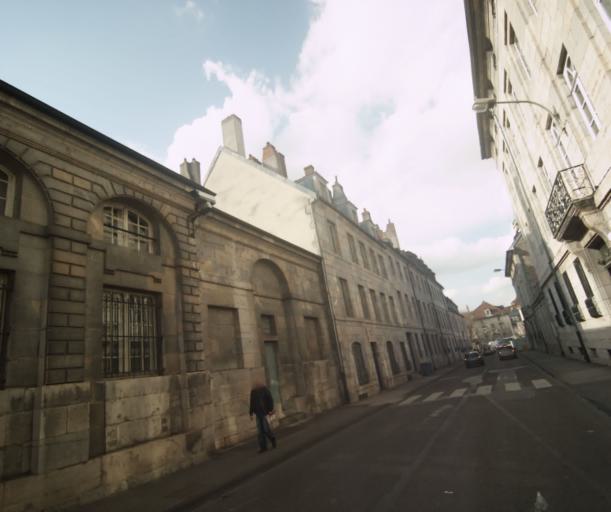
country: FR
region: Franche-Comte
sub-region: Departement du Doubs
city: Besancon
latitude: 47.2335
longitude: 6.0224
